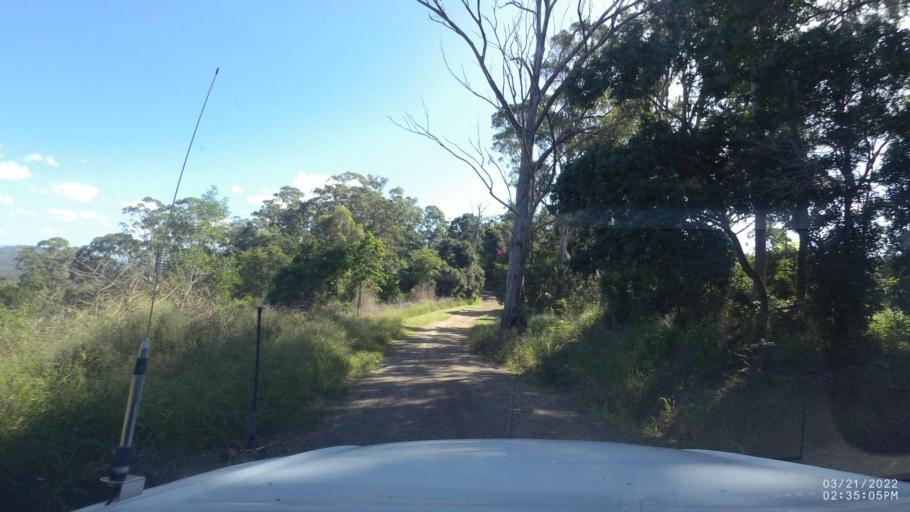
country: AU
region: Queensland
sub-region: Ipswich
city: Deebing Heights
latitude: -27.8287
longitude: 152.8210
